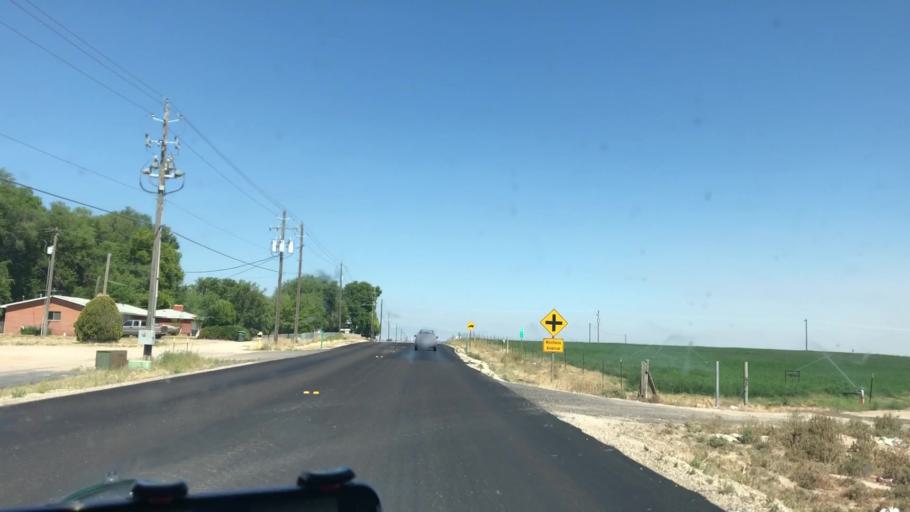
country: US
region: Idaho
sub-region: Canyon County
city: Caldwell
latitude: 43.6042
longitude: -116.6861
